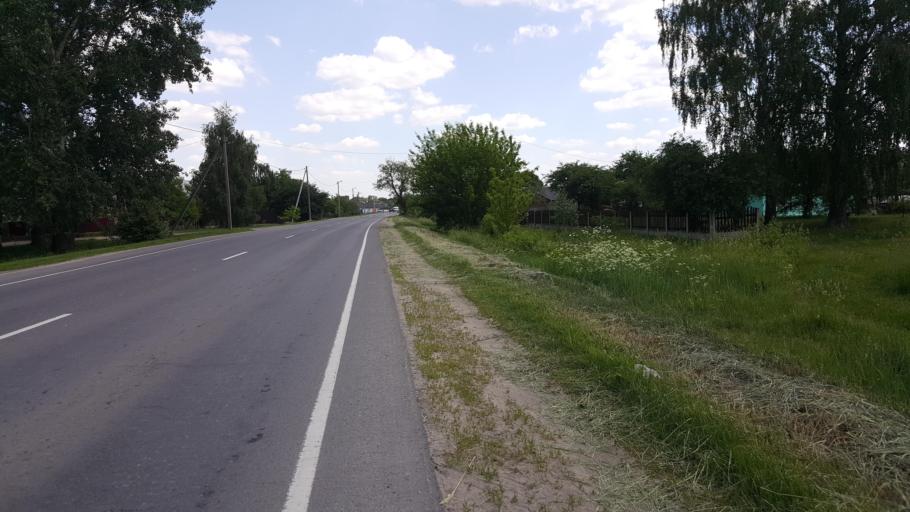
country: BY
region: Brest
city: Kobryn
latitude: 52.2268
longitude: 24.3228
